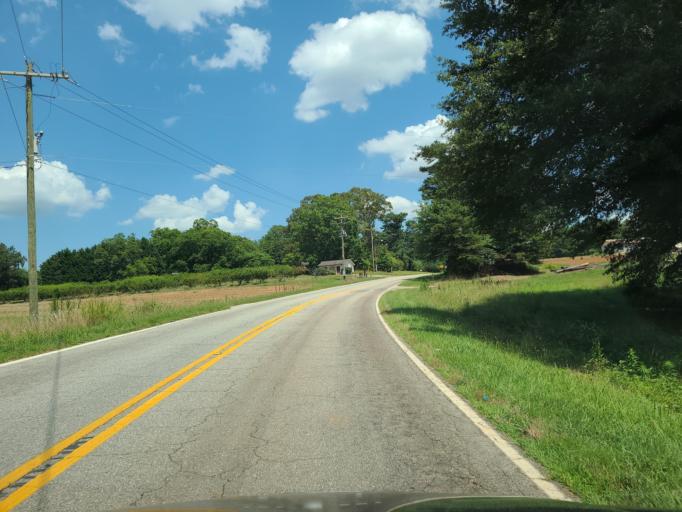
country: US
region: South Carolina
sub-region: Spartanburg County
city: Inman Mills
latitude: 35.0371
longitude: -82.1331
